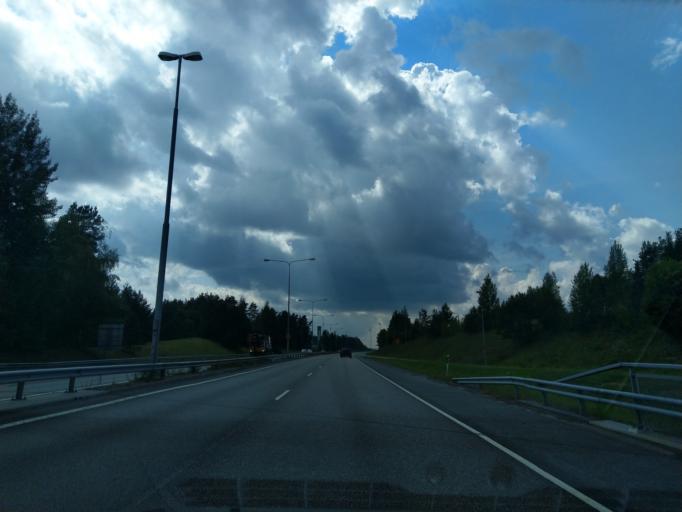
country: FI
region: South Karelia
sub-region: Imatra
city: Imatra
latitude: 61.1930
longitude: 28.7724
